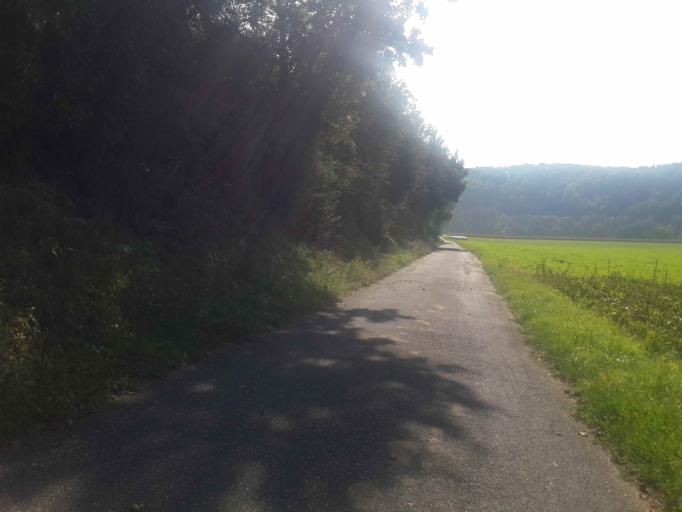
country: DE
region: Baden-Wuerttemberg
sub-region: Regierungsbezirk Stuttgart
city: Neudenau
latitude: 49.2981
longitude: 9.3177
